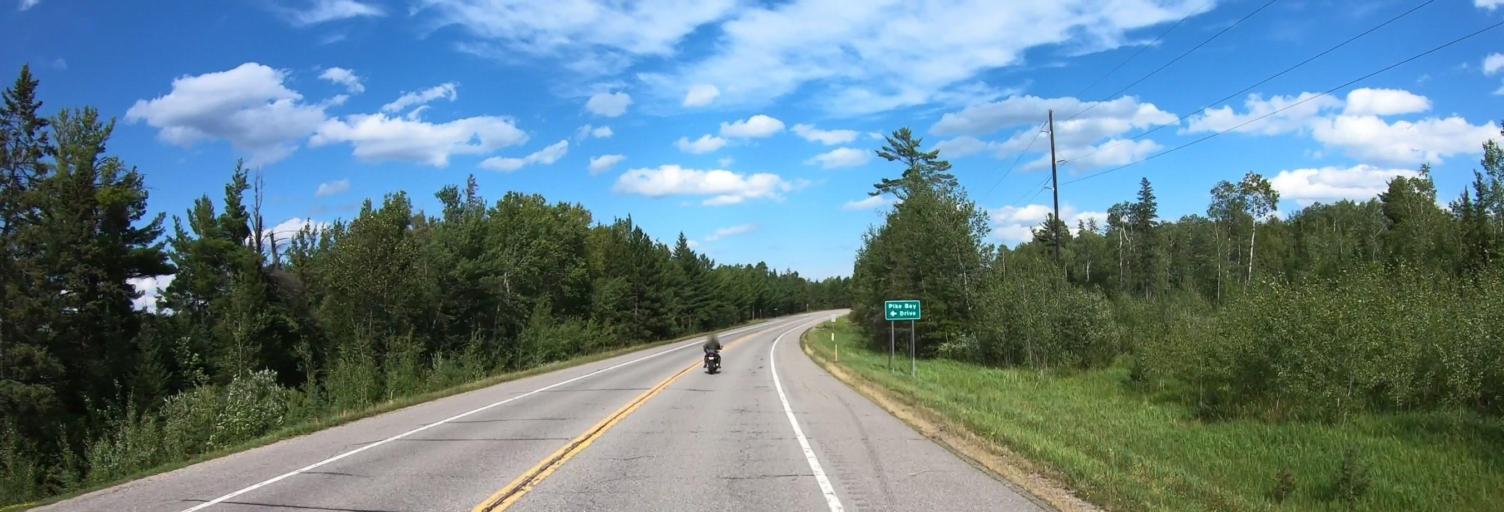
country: US
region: Minnesota
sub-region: Saint Louis County
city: Aurora
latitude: 47.7966
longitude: -92.3356
